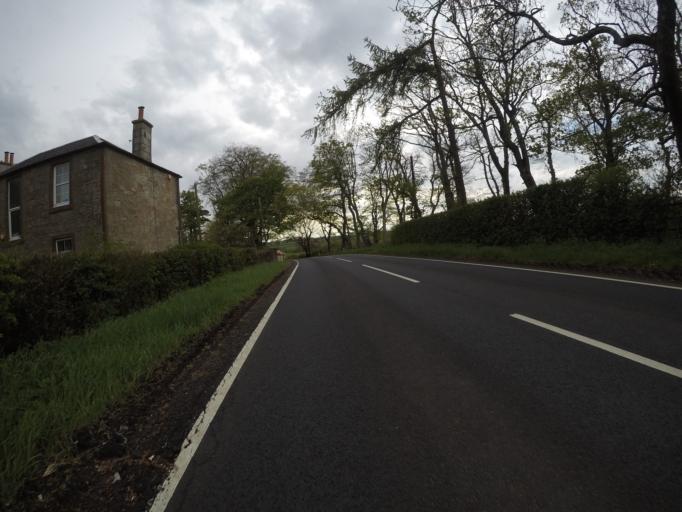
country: GB
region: Scotland
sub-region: East Ayrshire
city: Kilmaurs
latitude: 55.6430
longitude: -4.5111
